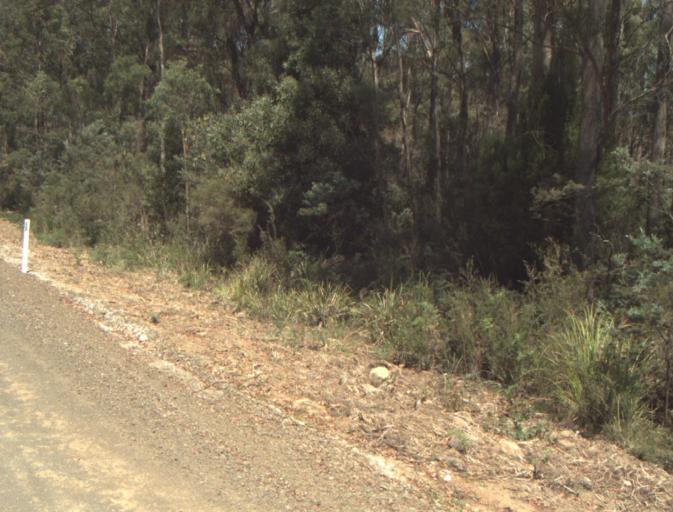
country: AU
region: Tasmania
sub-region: Launceston
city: Mayfield
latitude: -41.2784
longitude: 147.1167
